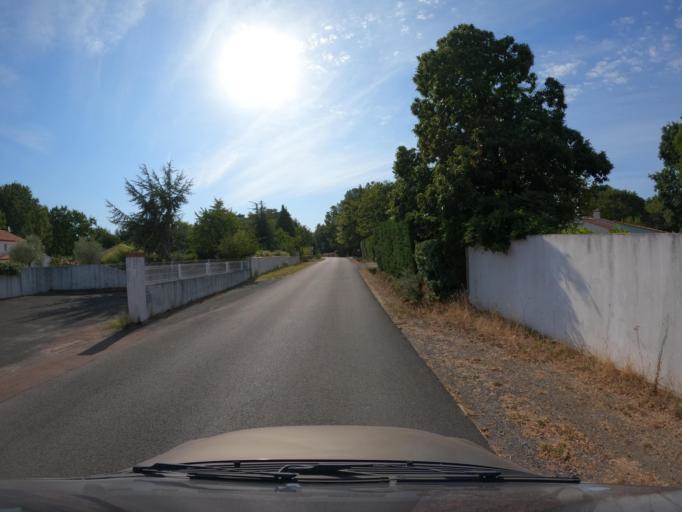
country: FR
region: Pays de la Loire
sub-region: Departement de la Vendee
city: Soullans
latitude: 46.8054
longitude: -1.8796
